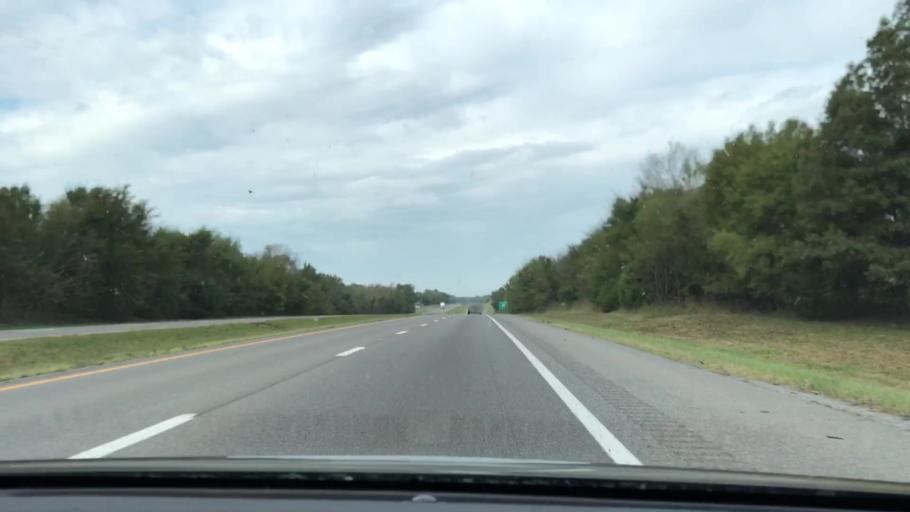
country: US
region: Kentucky
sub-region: Graves County
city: Mayfield
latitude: 36.7791
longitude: -88.5714
